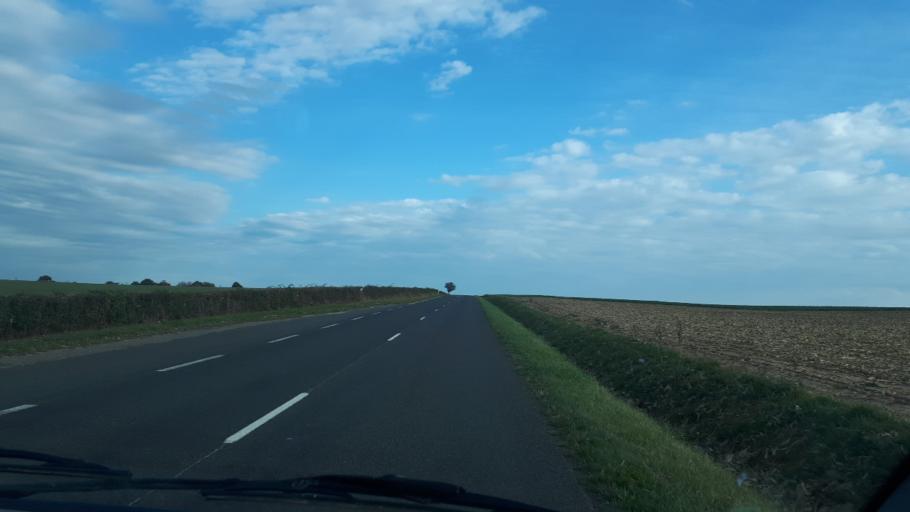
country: FR
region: Centre
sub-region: Departement du Loir-et-Cher
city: Mondoubleau
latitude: 47.9109
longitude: 0.9309
